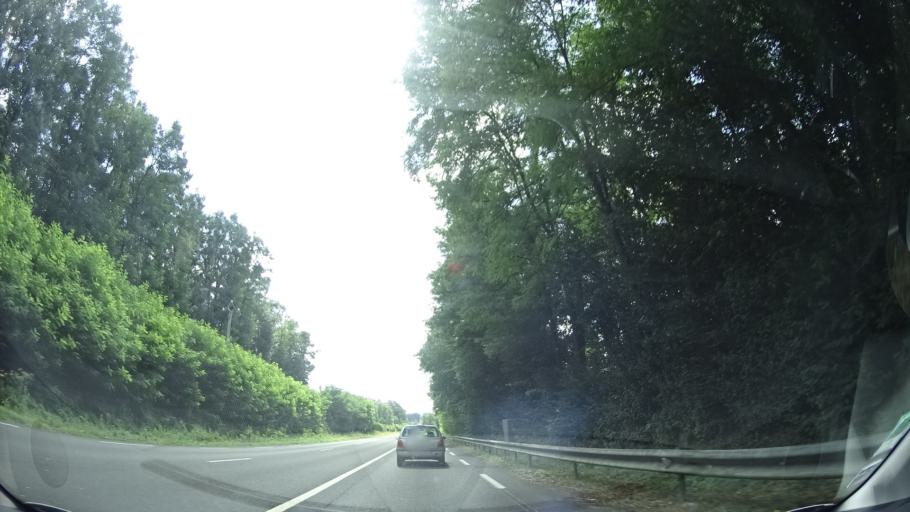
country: FR
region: Pays de la Loire
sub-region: Departement de la Sarthe
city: La Fleche
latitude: 47.7278
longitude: -0.1137
